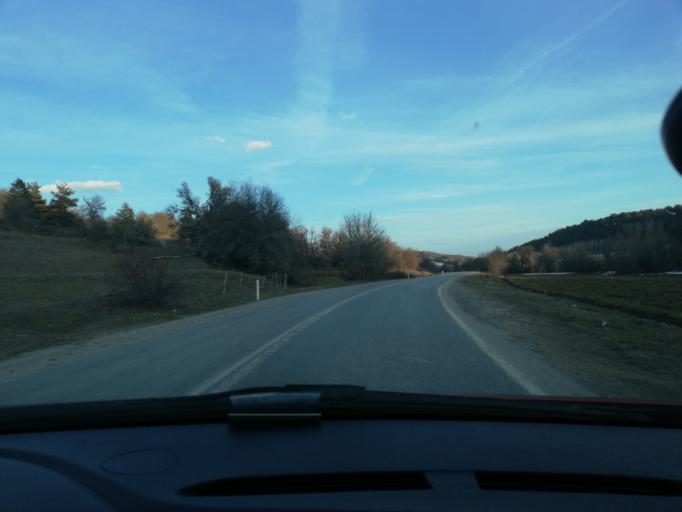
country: TR
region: Kastamonu
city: Agli
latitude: 41.6928
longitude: 33.5854
